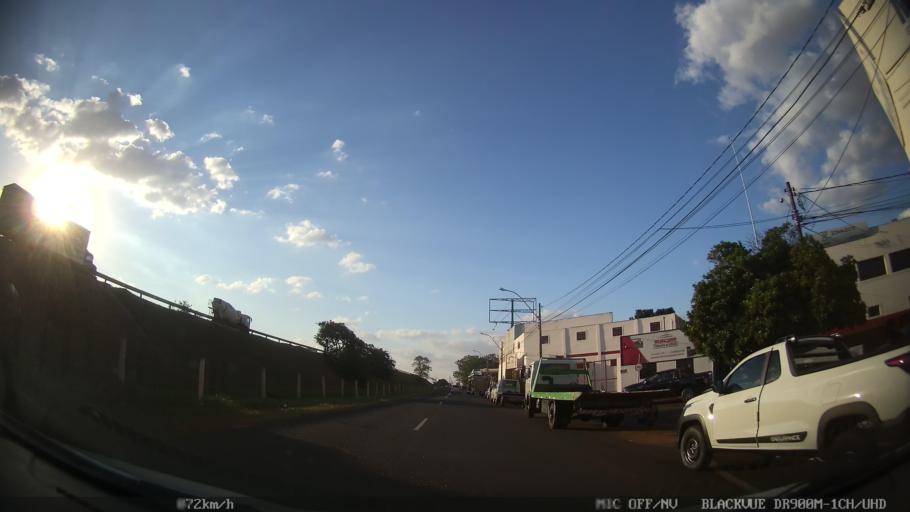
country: BR
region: Sao Paulo
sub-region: Ribeirao Preto
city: Ribeirao Preto
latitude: -21.1905
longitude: -47.7571
